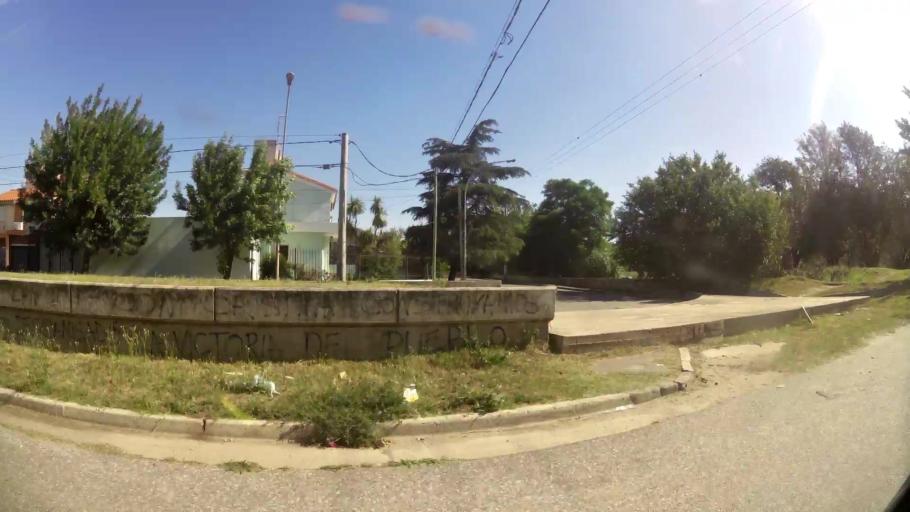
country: AR
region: Cordoba
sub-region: Departamento de Capital
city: Cordoba
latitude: -31.3583
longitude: -64.1860
